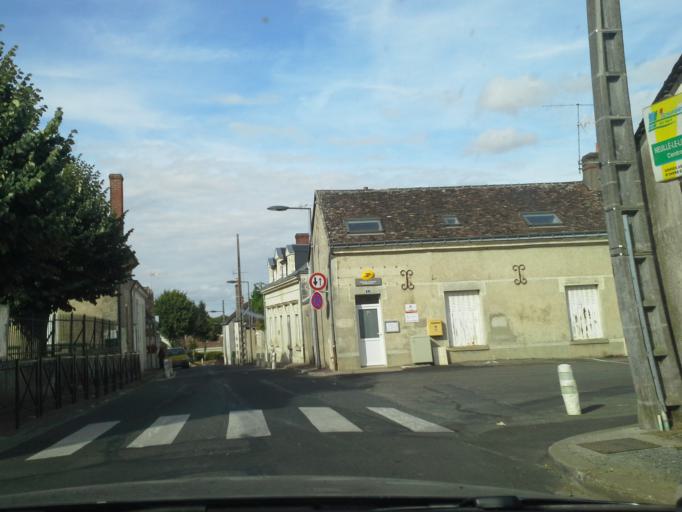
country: FR
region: Centre
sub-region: Departement d'Indre-et-Loire
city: Auzouer-en-Touraine
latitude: 47.5126
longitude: 0.9104
